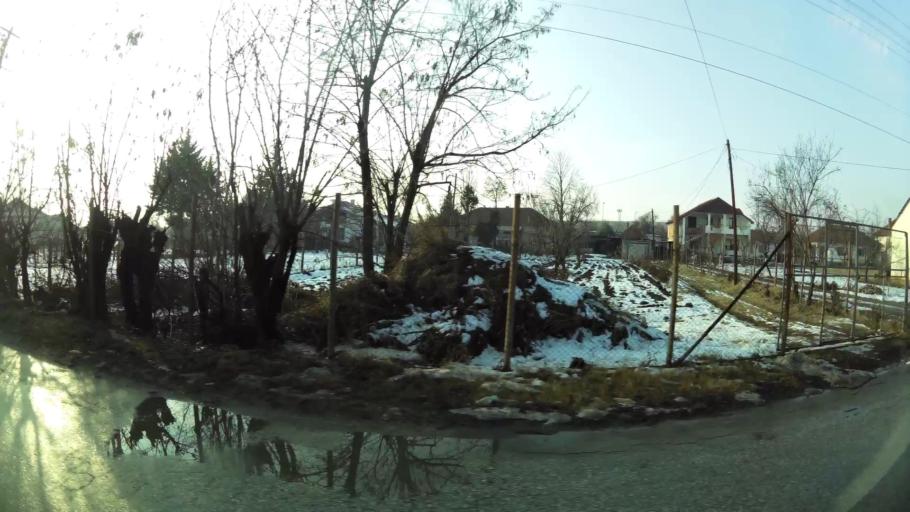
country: MK
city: Miladinovci
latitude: 41.9880
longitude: 21.6522
